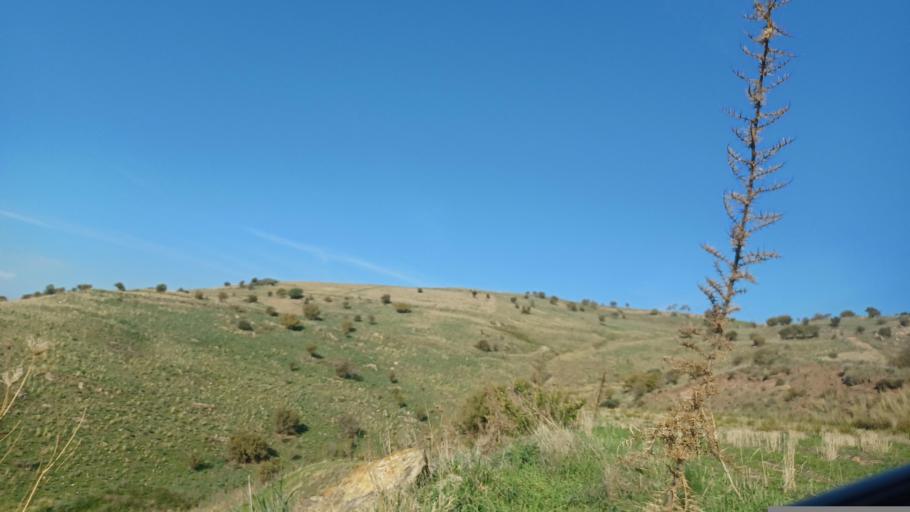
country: CY
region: Pafos
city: Mesogi
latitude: 34.7729
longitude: 32.5463
